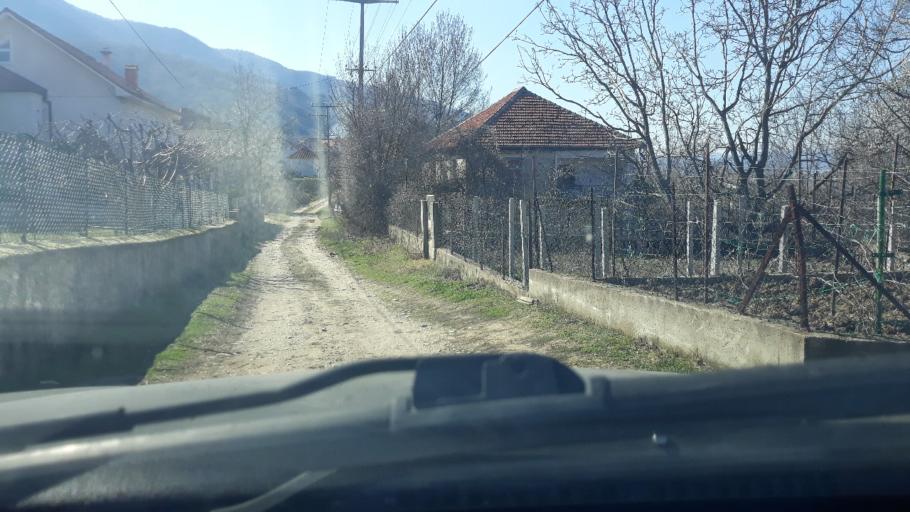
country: MK
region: Novo Selo
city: Novo Selo
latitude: 41.3762
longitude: 22.8429
